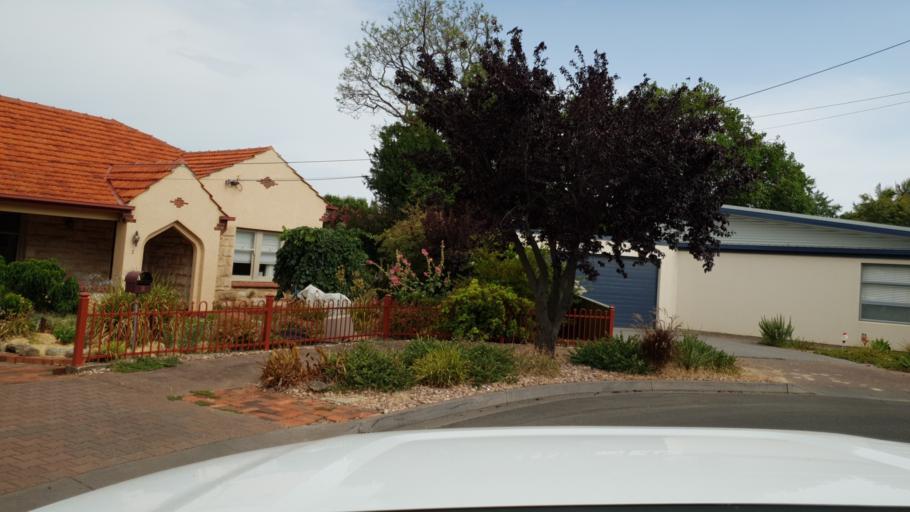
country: AU
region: South Australia
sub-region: Mitcham
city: Clarence Gardens
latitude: -34.9711
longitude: 138.5812
